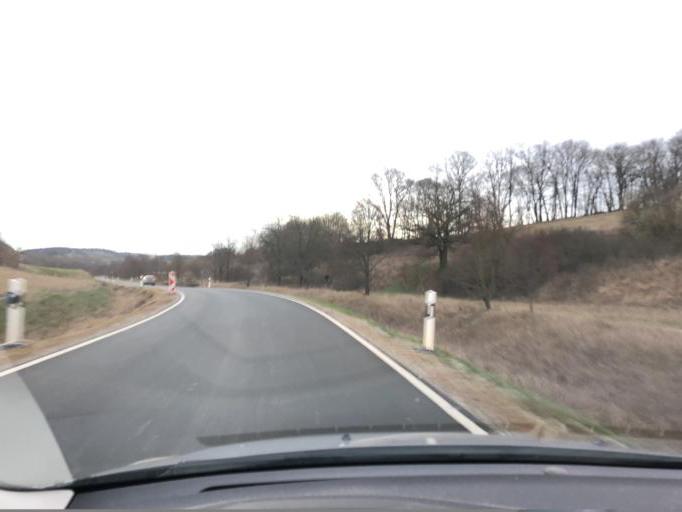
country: DE
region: Saxony-Anhalt
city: Balgstadt
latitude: 51.2051
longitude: 11.7176
